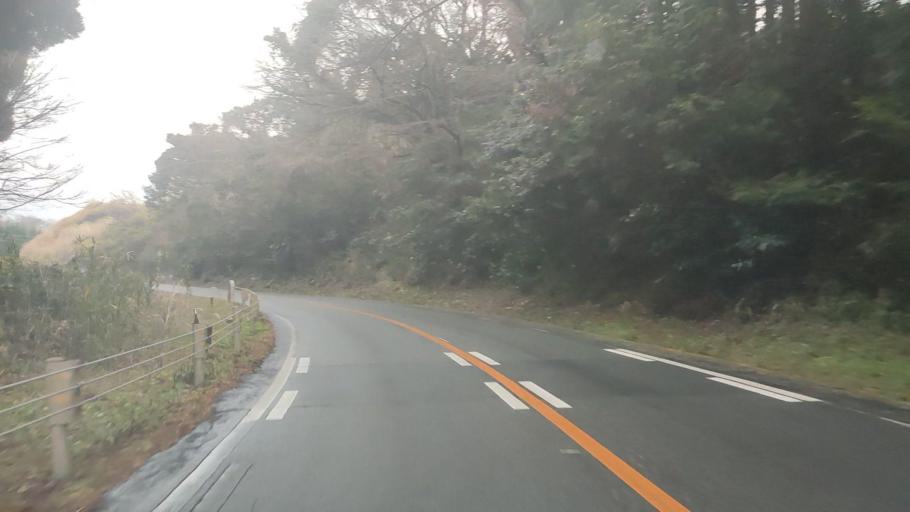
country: JP
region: Kumamoto
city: Aso
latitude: 32.8965
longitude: 130.9988
